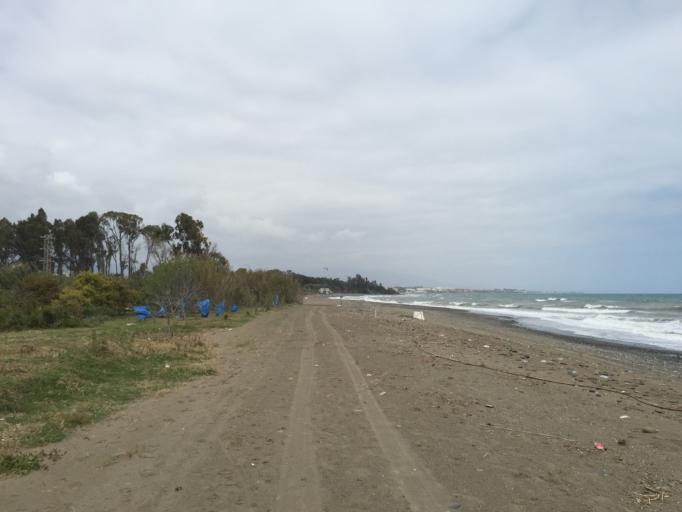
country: ES
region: Andalusia
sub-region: Provincia de Malaga
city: Estepona
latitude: 36.4358
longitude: -5.1066
